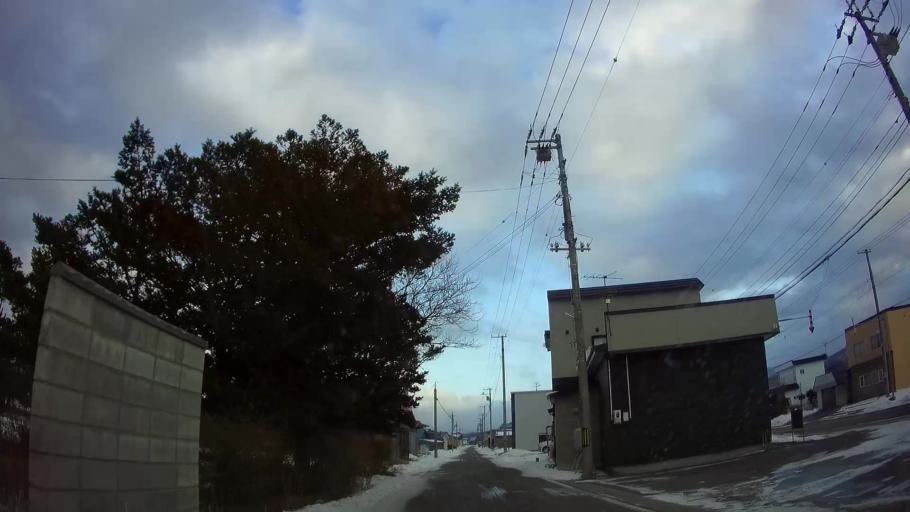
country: JP
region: Hokkaido
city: Nanae
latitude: 42.0443
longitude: 140.8114
